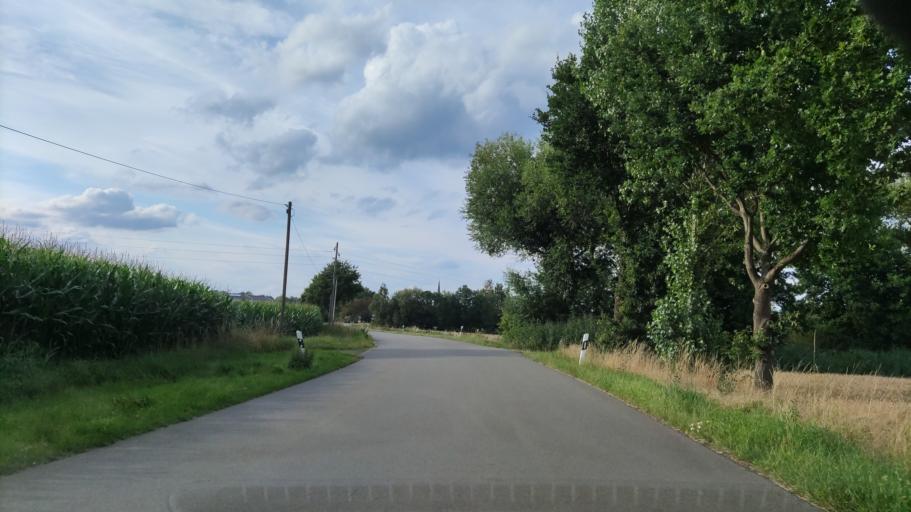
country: DE
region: Lower Saxony
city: Dannenberg
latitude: 53.0924
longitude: 11.0981
